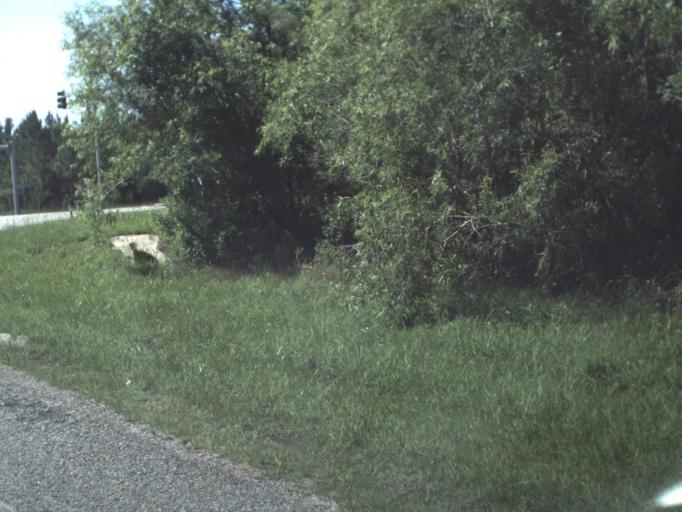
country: US
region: Florida
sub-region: Duval County
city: Jacksonville
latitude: 30.4667
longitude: -81.6711
